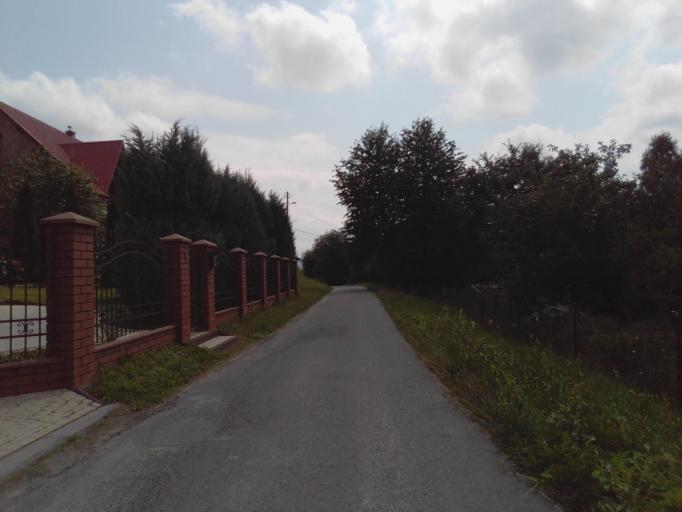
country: PL
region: Subcarpathian Voivodeship
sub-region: Powiat strzyzowski
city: Czudec
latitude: 49.9465
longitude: 21.8325
